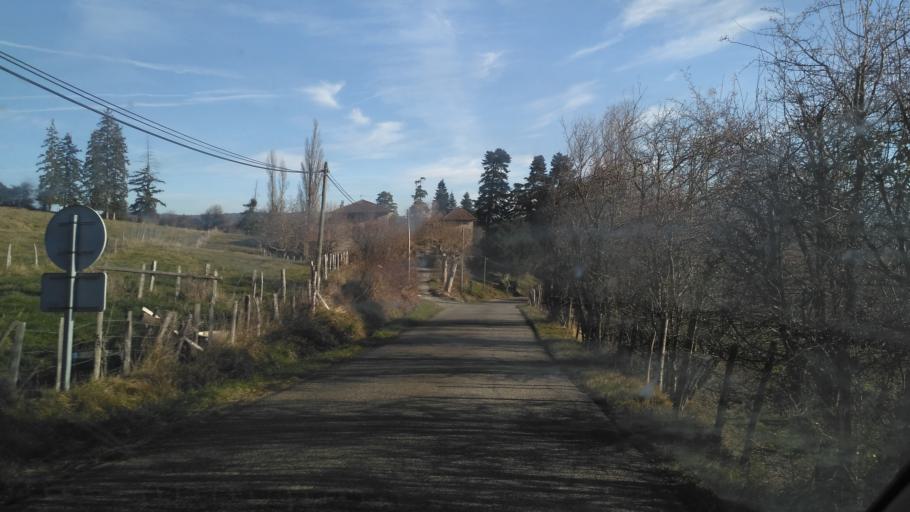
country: FR
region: Rhone-Alpes
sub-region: Departement de l'Isere
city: Saint-Antoine-l'Abbaye
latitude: 45.1753
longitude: 5.2013
